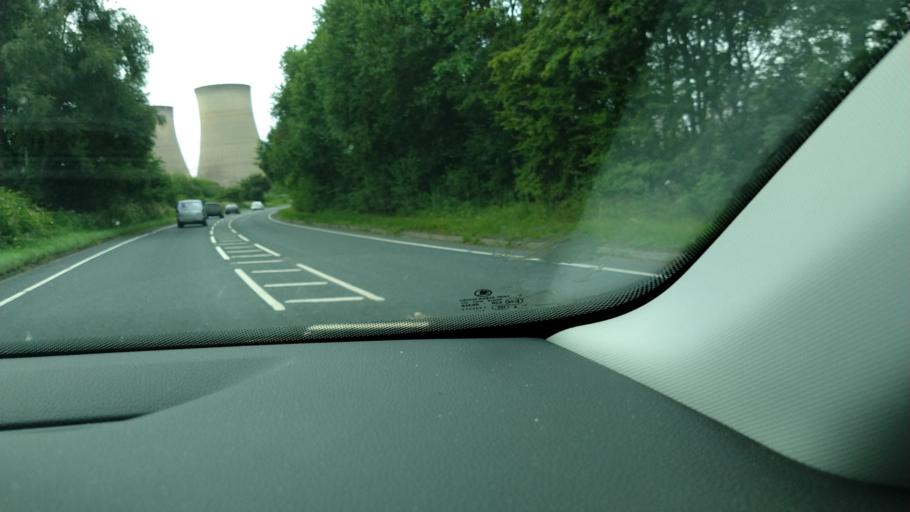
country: GB
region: England
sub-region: North Yorkshire
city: Camblesforth
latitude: 53.7259
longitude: -0.9898
